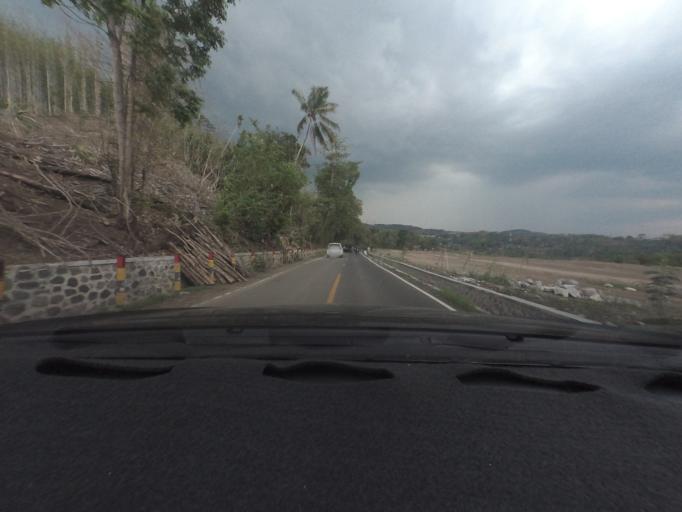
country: ID
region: West Java
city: Sindangsari
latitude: -6.9945
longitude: 106.6646
